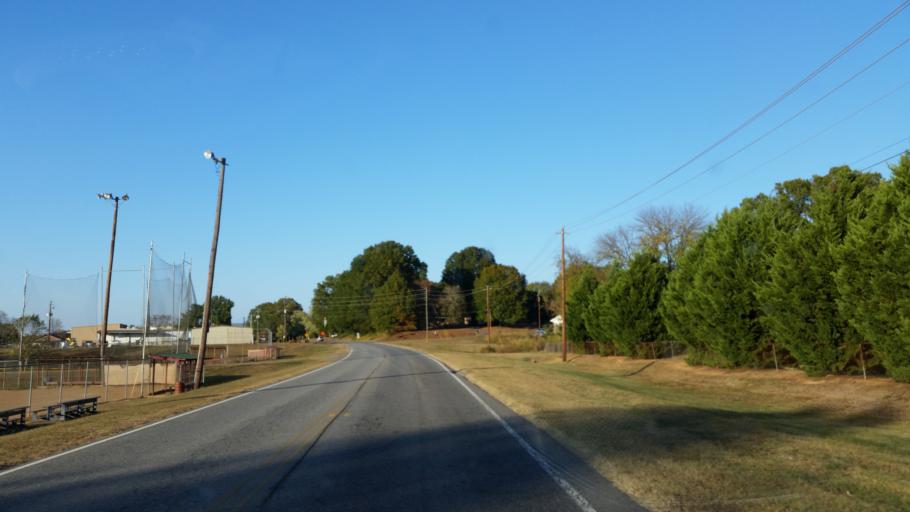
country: US
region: Georgia
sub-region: Bartow County
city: Adairsville
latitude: 34.3717
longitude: -84.9410
